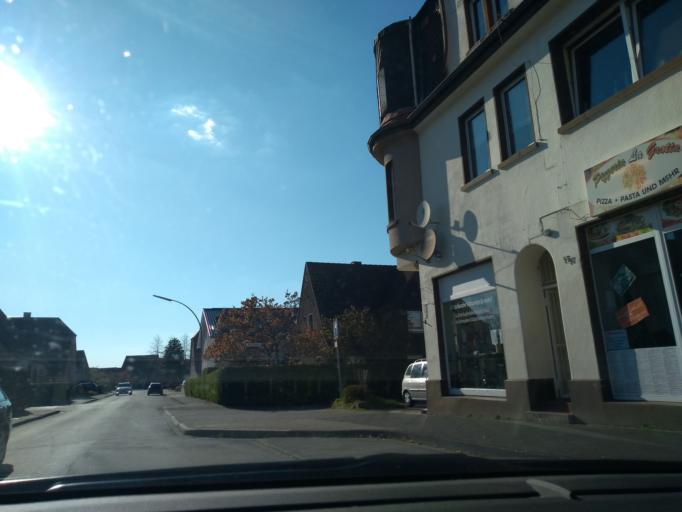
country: DE
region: North Rhine-Westphalia
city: Selm
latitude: 51.6921
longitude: 7.4708
